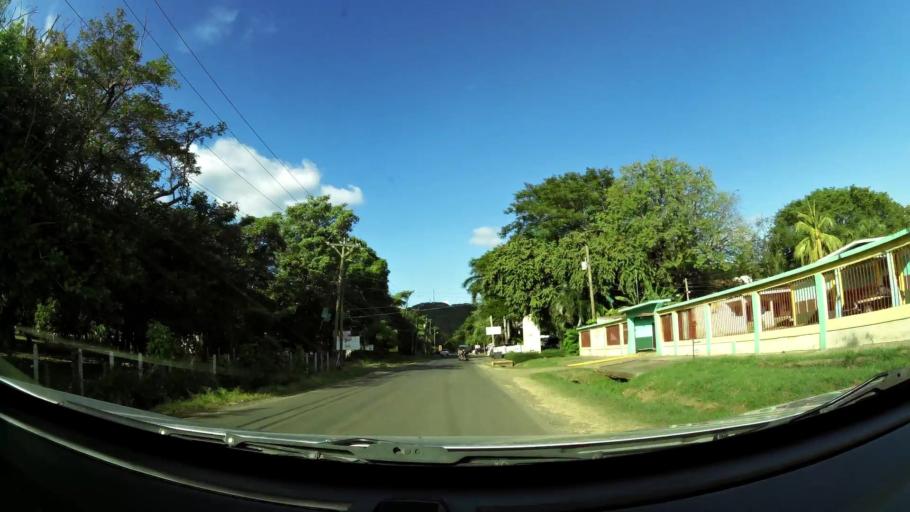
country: CR
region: Guanacaste
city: Sardinal
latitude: 10.5535
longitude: -85.6931
